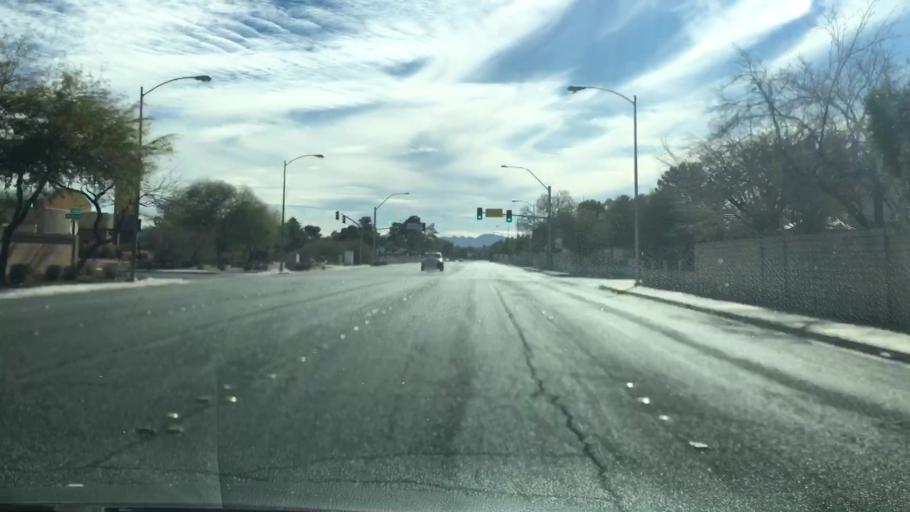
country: US
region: Nevada
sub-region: Clark County
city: Paradise
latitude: 36.0540
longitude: -115.1409
